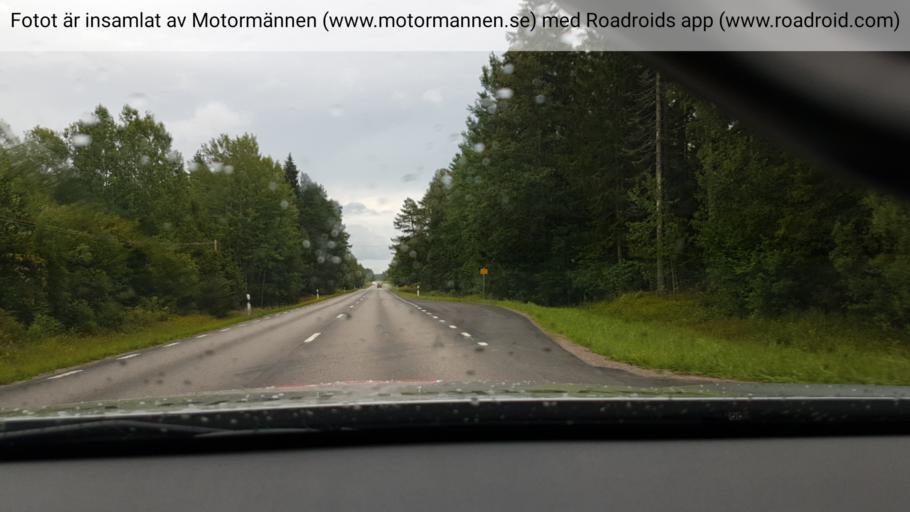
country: SE
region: Uppsala
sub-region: Tierps Kommun
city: Karlholmsbruk
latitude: 60.5420
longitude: 17.5483
